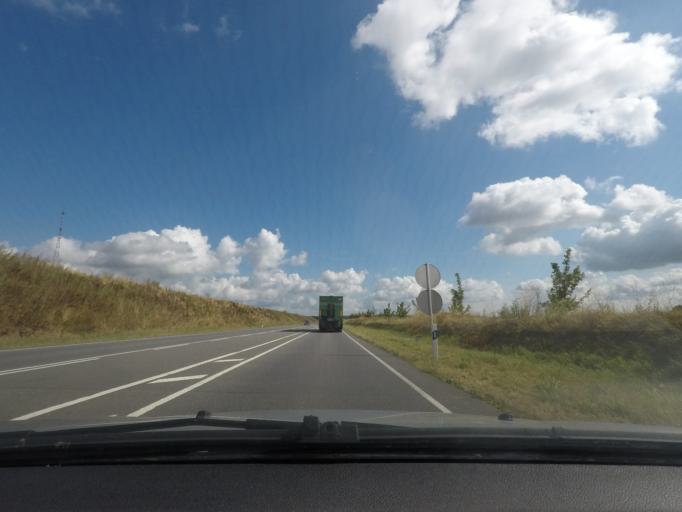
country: LU
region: Grevenmacher
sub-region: Canton de Grevenmacher
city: Junglinster
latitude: 49.7124
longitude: 6.2665
